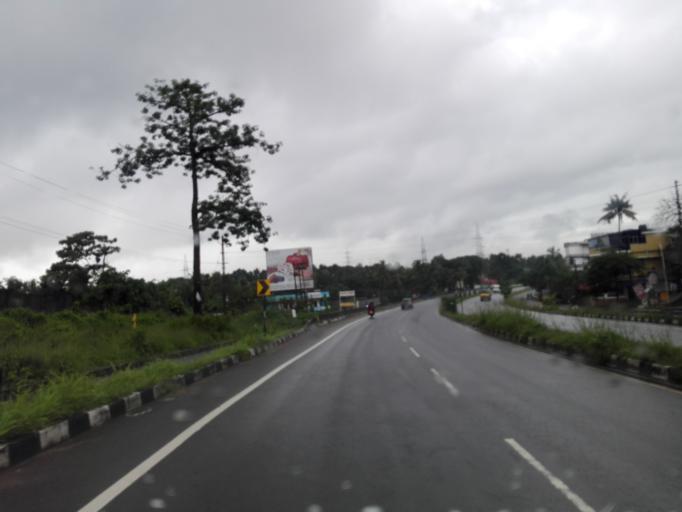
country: IN
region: Kerala
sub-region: Ernakulam
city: Elur
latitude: 10.0708
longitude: 76.3195
